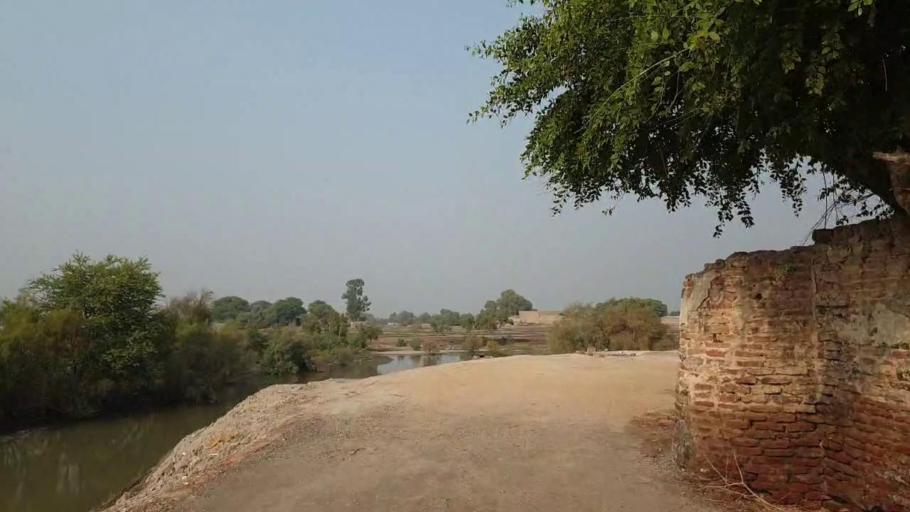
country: PK
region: Sindh
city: Bhan
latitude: 26.4600
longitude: 67.7122
